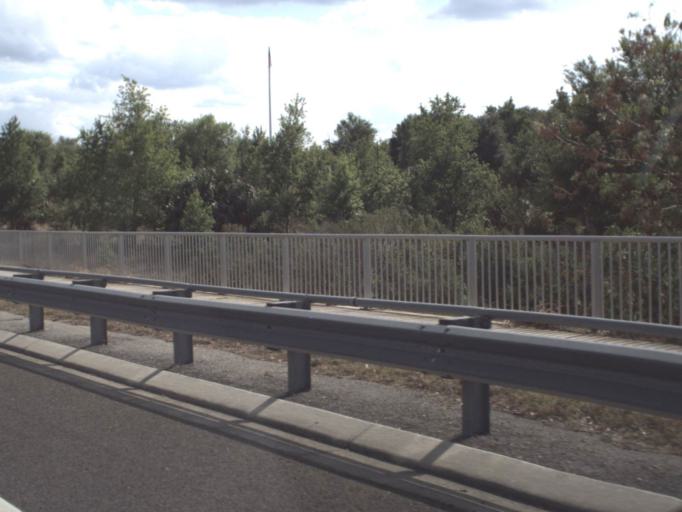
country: US
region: Florida
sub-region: Lake County
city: Clermont
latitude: 28.5235
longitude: -81.7305
